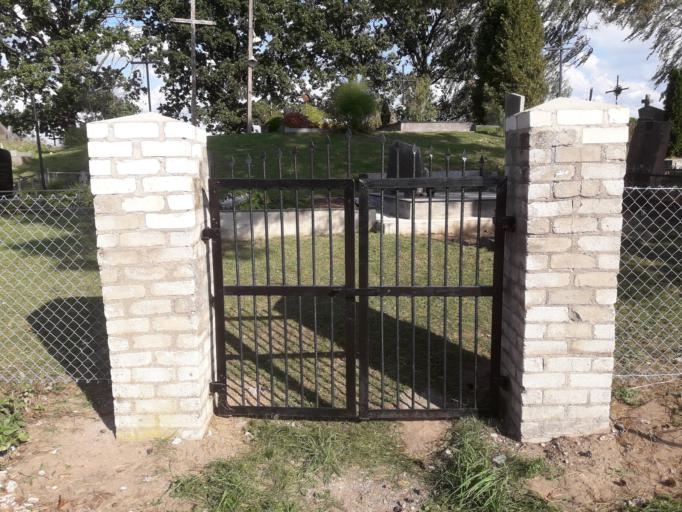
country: LT
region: Alytaus apskritis
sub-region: Alytaus rajonas
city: Daugai
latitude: 54.2356
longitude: 24.2253
